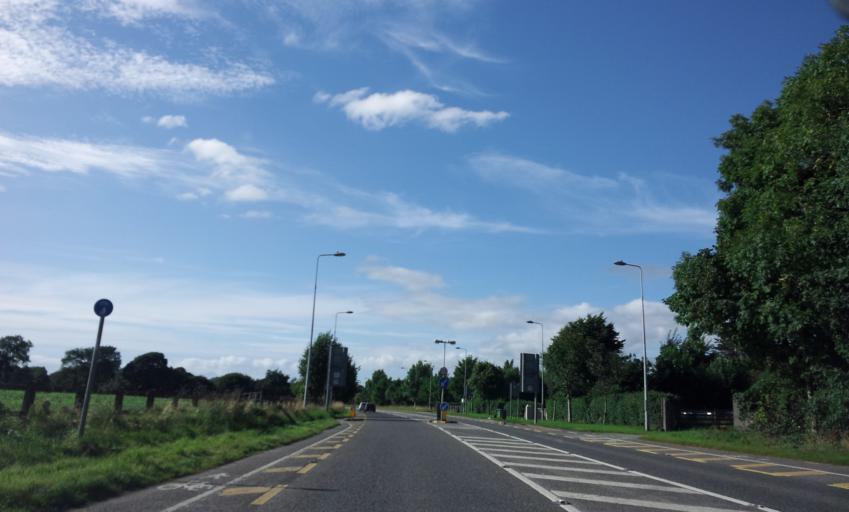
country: IE
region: Munster
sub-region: Ciarrai
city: Cill Airne
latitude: 52.0521
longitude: -9.4592
